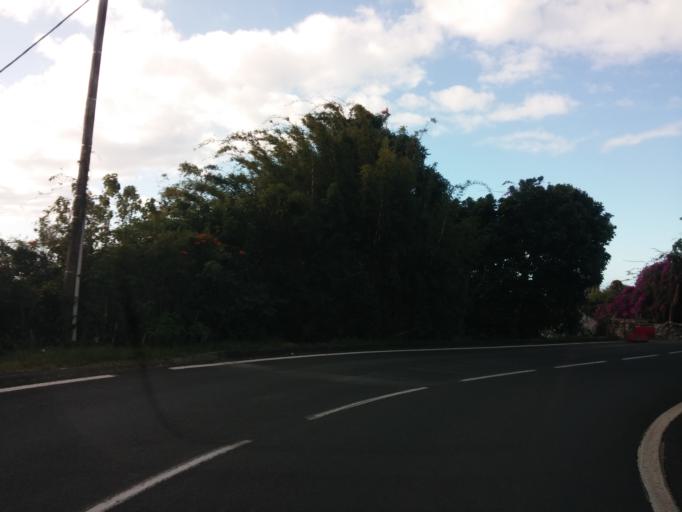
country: RE
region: Reunion
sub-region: Reunion
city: Saint-Denis
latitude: -20.8934
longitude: 55.4173
